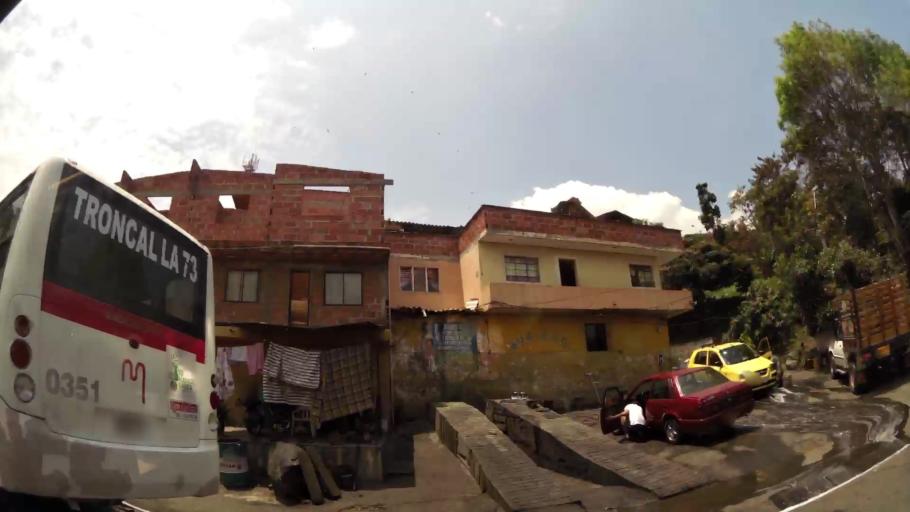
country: CO
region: Antioquia
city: Bello
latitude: 6.2985
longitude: -75.5788
